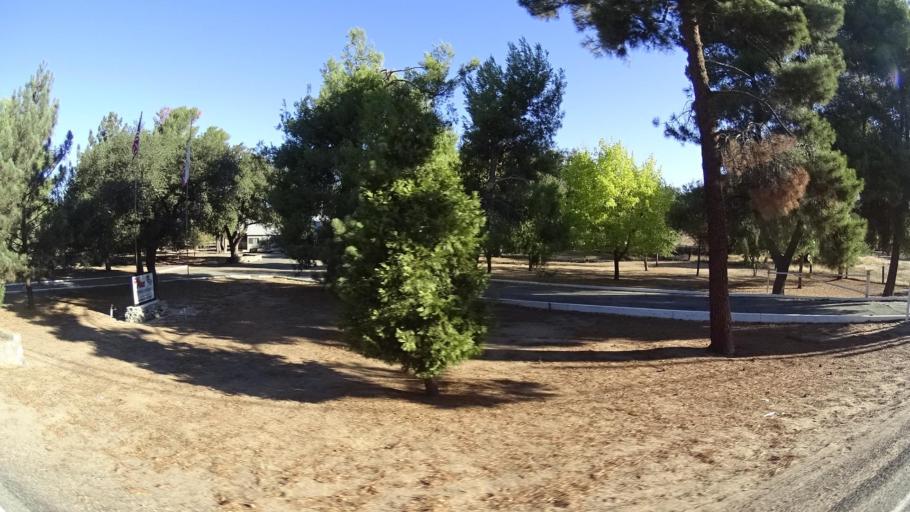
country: MX
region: Baja California
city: Tecate
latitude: 32.6045
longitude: -116.6088
